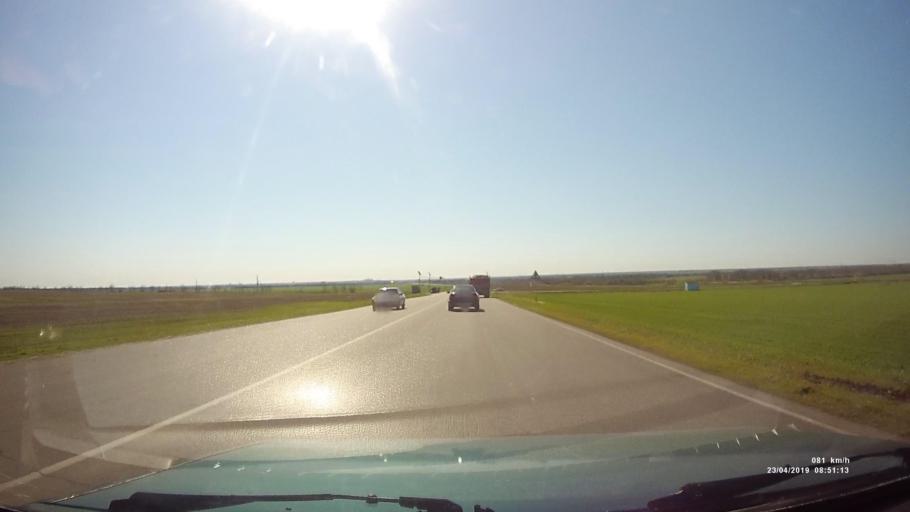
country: RU
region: Rostov
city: Gigant
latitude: 46.4905
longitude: 41.4396
